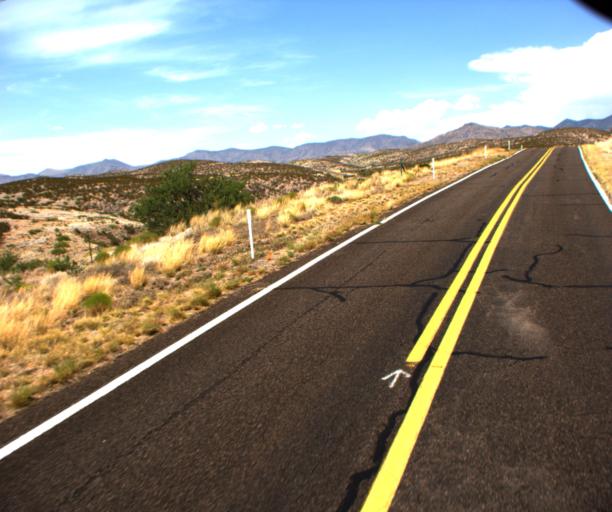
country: US
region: Arizona
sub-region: Greenlee County
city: Clifton
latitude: 32.9829
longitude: -109.1854
